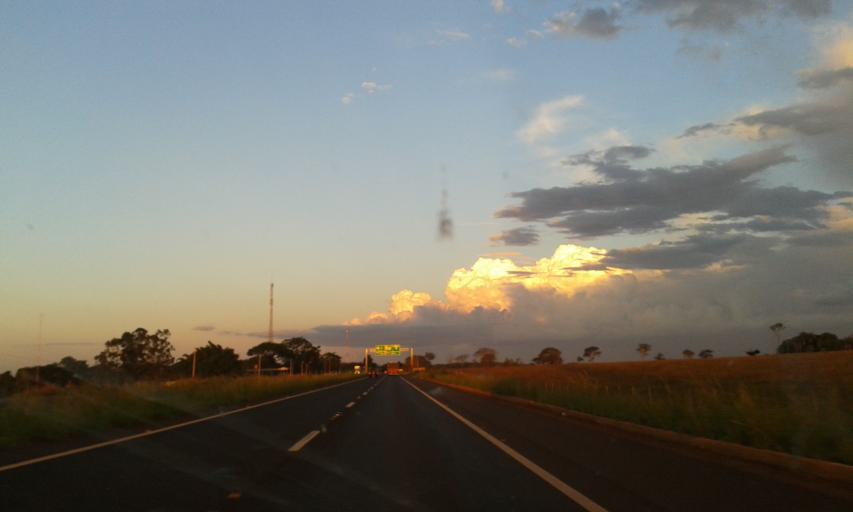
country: BR
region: Minas Gerais
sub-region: Monte Alegre De Minas
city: Monte Alegre de Minas
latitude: -18.8883
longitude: -48.7124
